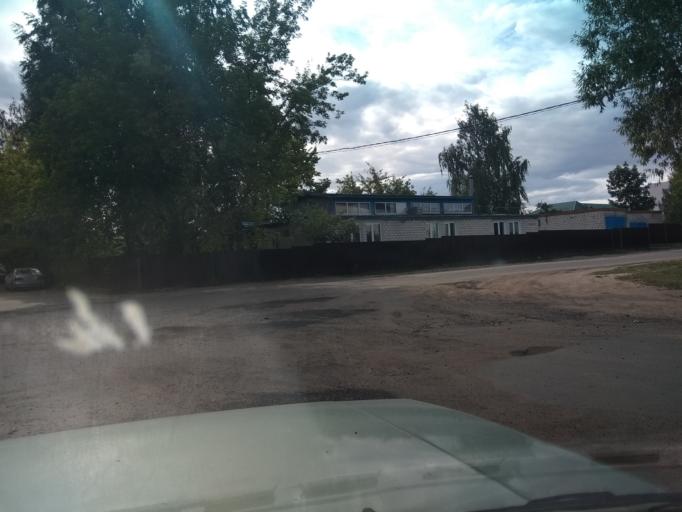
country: BY
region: Mogilev
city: Mahilyow
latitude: 53.9245
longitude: 30.3453
